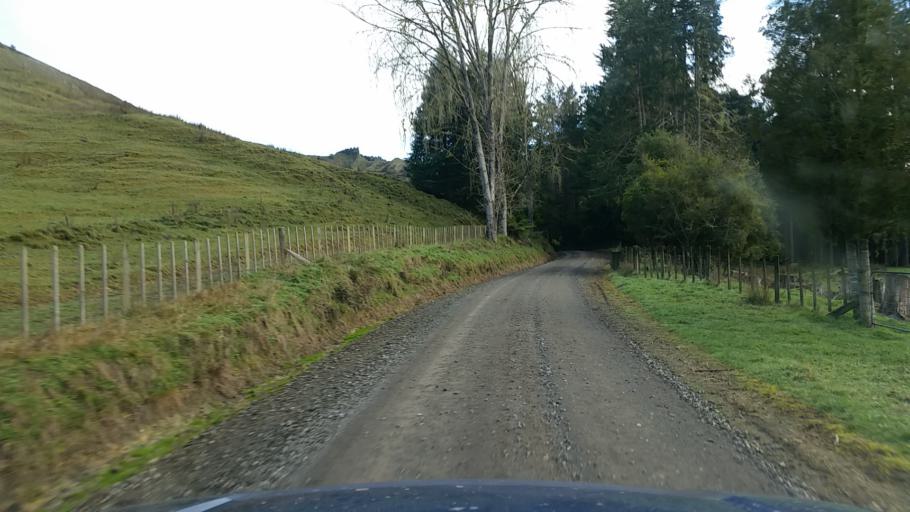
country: NZ
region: Taranaki
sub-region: New Plymouth District
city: Waitara
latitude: -39.1013
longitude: 174.8405
